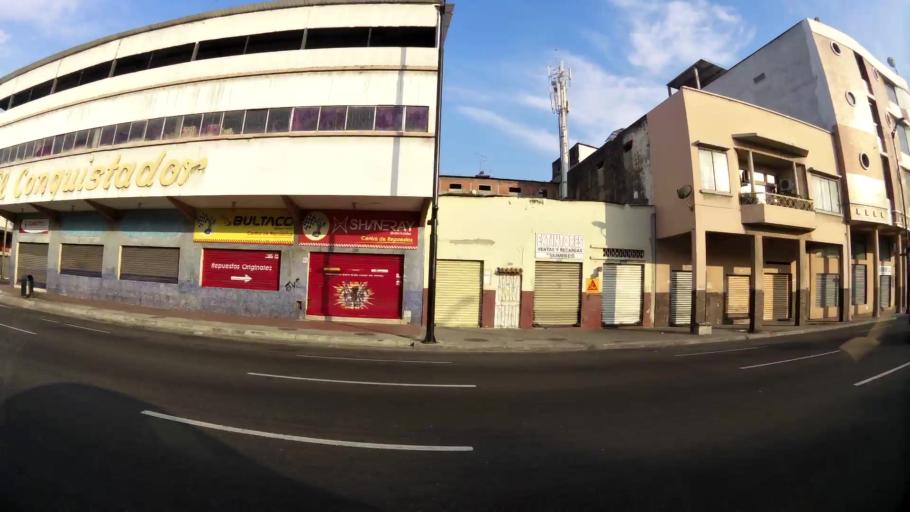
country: EC
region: Guayas
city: Guayaquil
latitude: -2.1970
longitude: -79.8915
